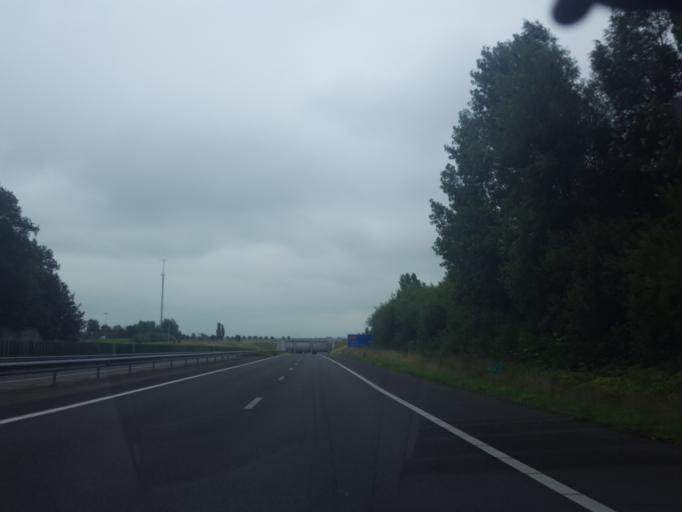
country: NL
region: Friesland
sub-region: Gemeente Boarnsterhim
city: Grou
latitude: 53.0840
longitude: 5.8262
